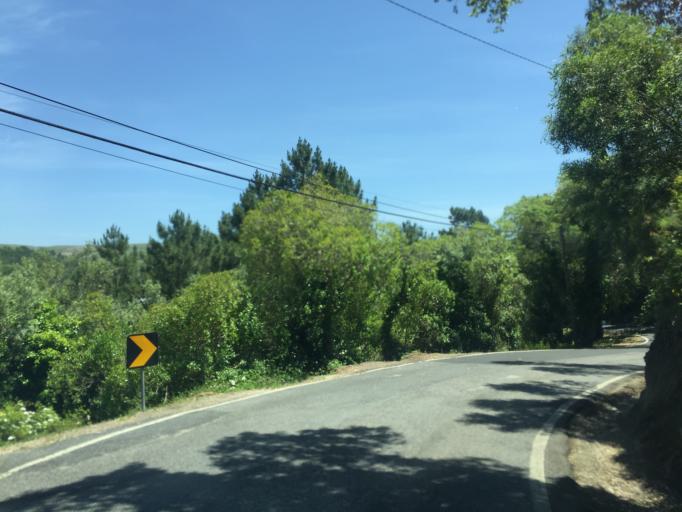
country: PT
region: Lisbon
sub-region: Mafra
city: Venda do Pinheiro
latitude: 38.8903
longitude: -9.2126
